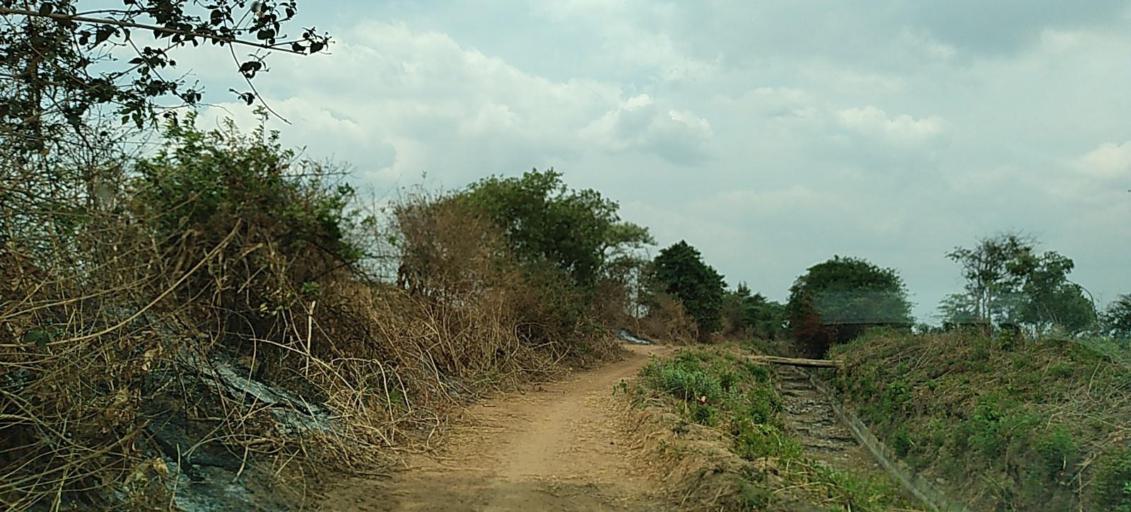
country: ZM
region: Copperbelt
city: Chililabombwe
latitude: -12.3613
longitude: 27.8004
